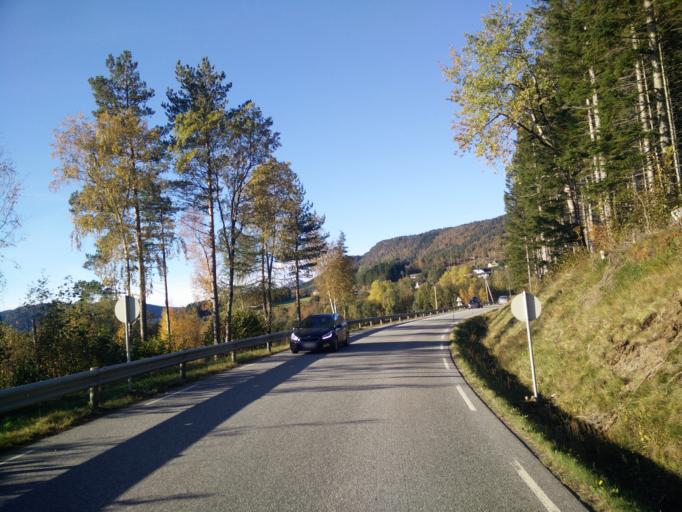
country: NO
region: More og Romsdal
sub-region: Halsa
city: Liaboen
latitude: 63.1135
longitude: 8.3231
